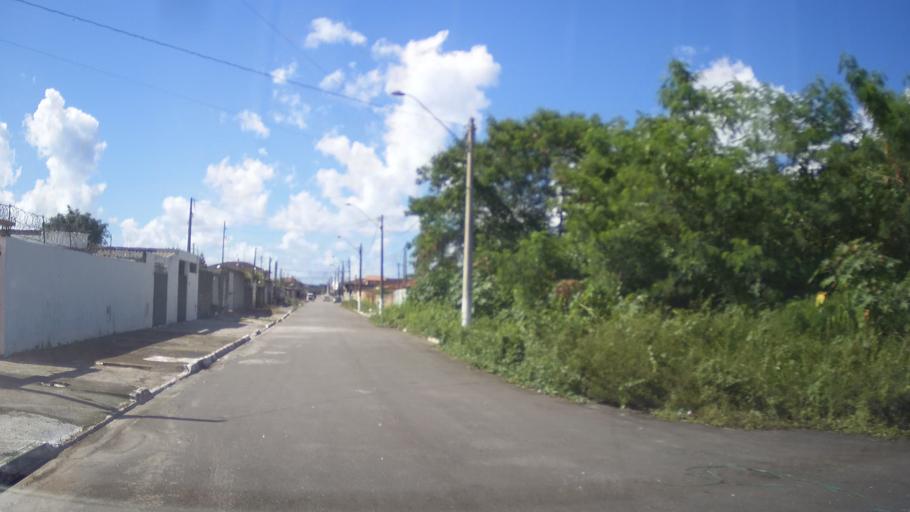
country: BR
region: Sao Paulo
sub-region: Praia Grande
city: Praia Grande
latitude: -24.0209
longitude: -46.5132
